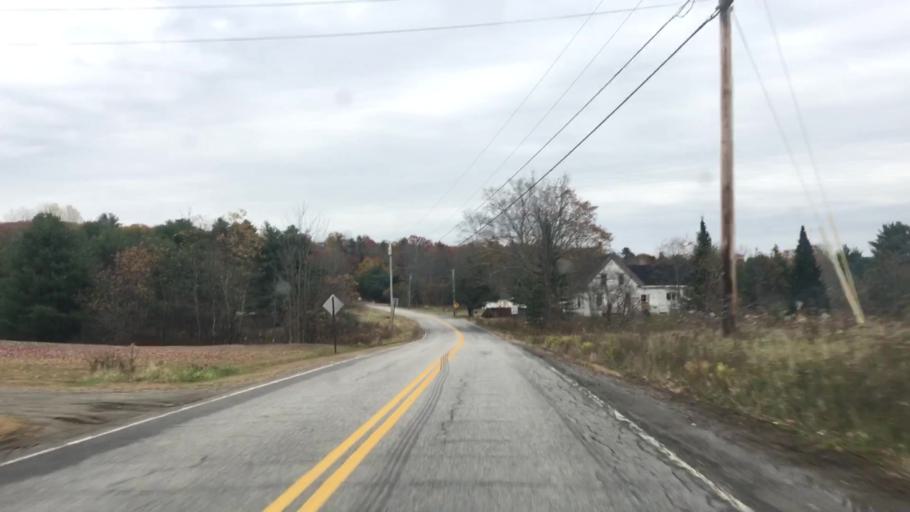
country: US
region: Maine
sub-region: Lincoln County
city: Whitefield
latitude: 44.1729
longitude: -69.6723
